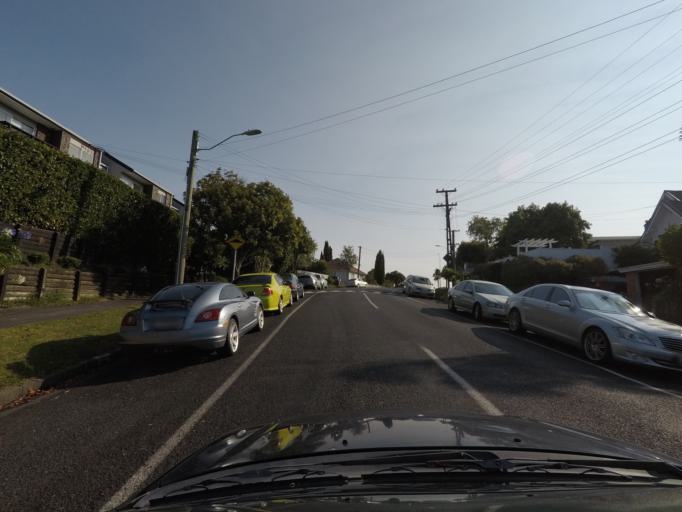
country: NZ
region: Auckland
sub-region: Auckland
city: Auckland
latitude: -36.9004
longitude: 174.7375
